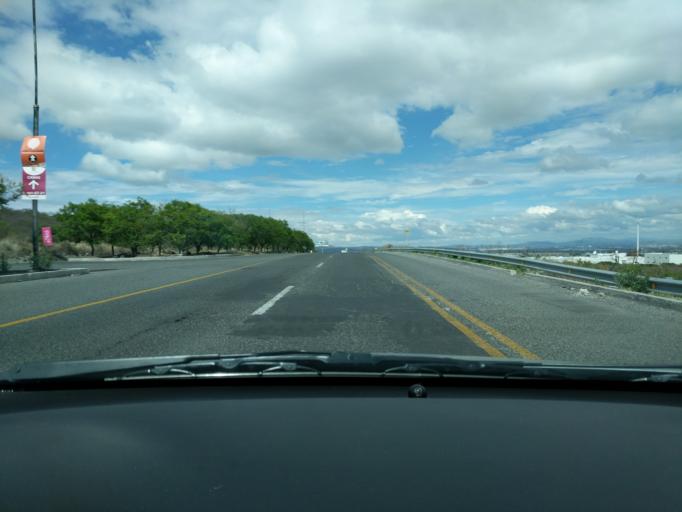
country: MX
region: Queretaro
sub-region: El Marques
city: La Pradera
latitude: 20.6623
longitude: -100.3365
